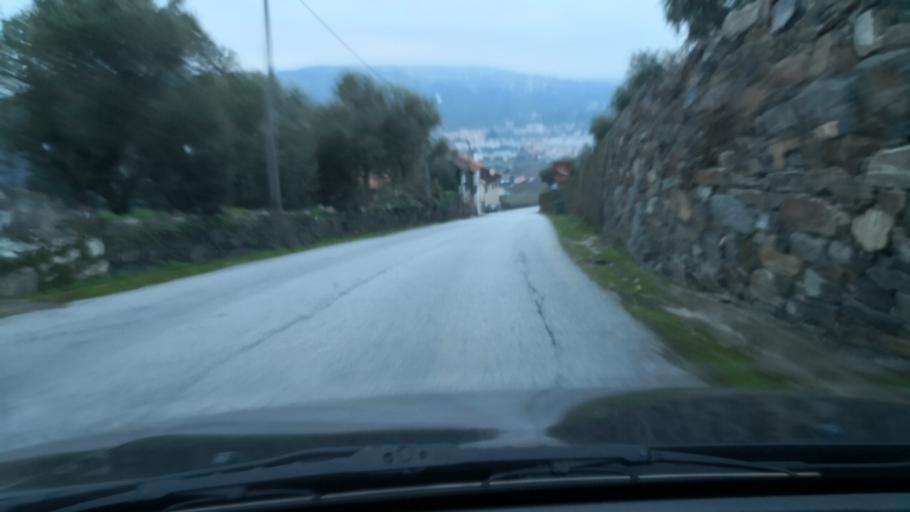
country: PT
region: Vila Real
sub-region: Peso da Regua
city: Peso da Regua
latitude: 41.1434
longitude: -7.7916
